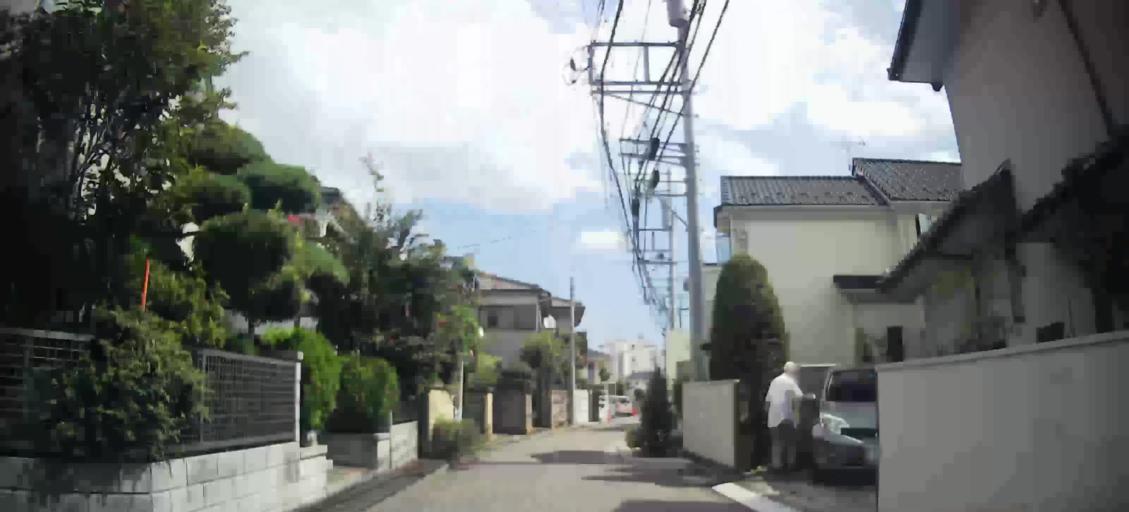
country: JP
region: Kanagawa
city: Yokohama
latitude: 35.4864
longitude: 139.5504
